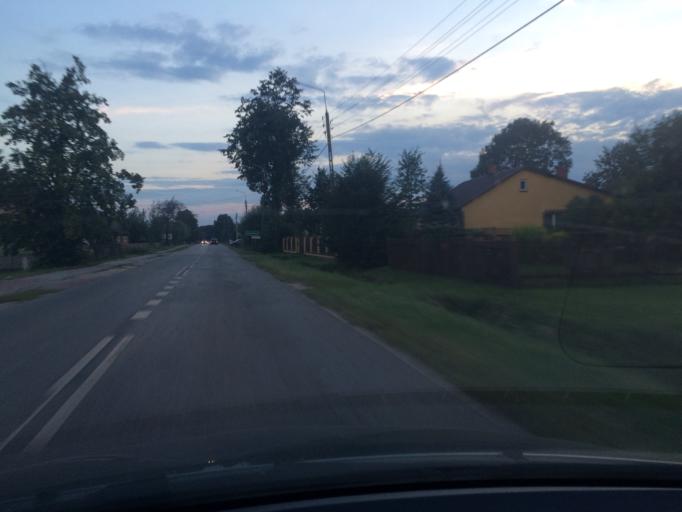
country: PL
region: Swietokrzyskie
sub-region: Powiat skarzyski
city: Suchedniow
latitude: 51.0484
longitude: 20.8929
